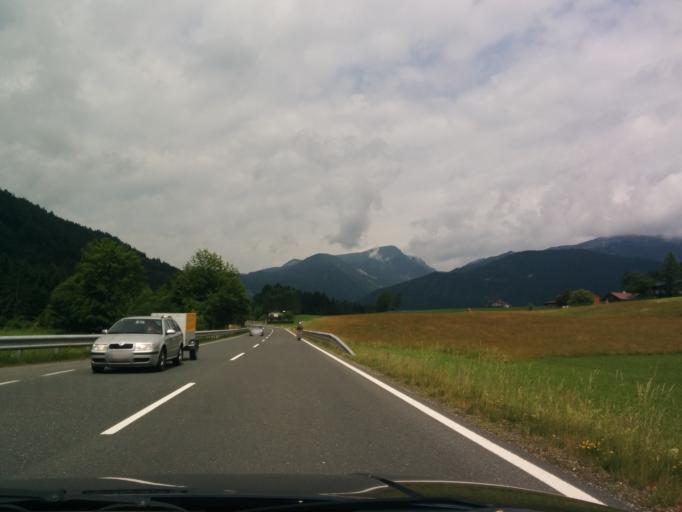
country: AT
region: Salzburg
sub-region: Politischer Bezirk Hallein
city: Abtenau
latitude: 47.5775
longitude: 13.3259
